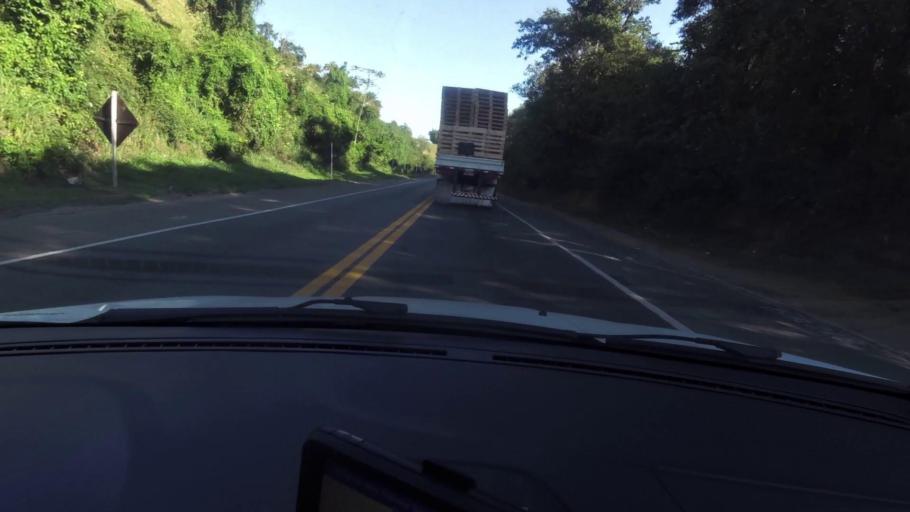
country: BR
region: Espirito Santo
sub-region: Alfredo Chaves
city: Alfredo Chaves
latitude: -20.6681
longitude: -40.6630
